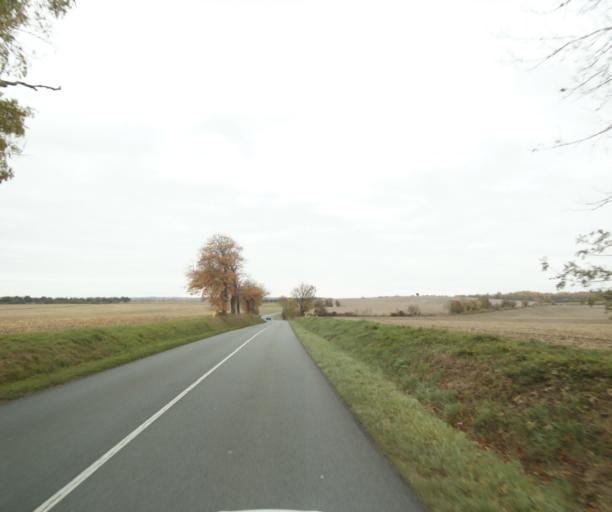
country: FR
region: Poitou-Charentes
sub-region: Departement de la Charente-Maritime
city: Les Gonds
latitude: 45.7135
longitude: -0.6447
